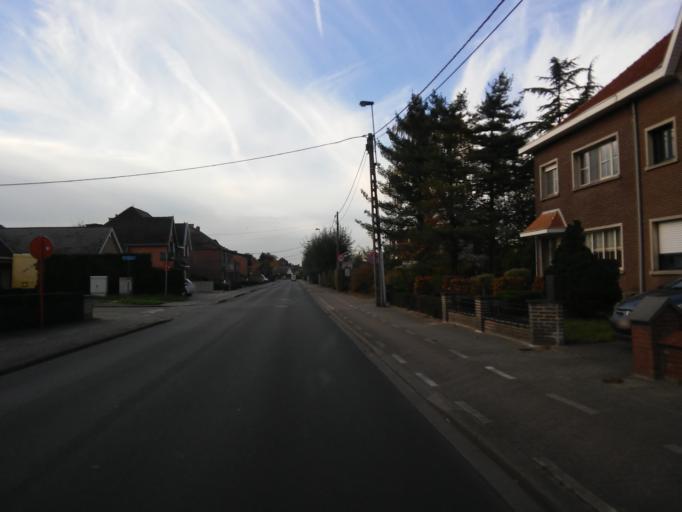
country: BE
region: Flanders
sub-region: Provincie Oost-Vlaanderen
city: Buggenhout
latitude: 51.0203
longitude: 4.1988
